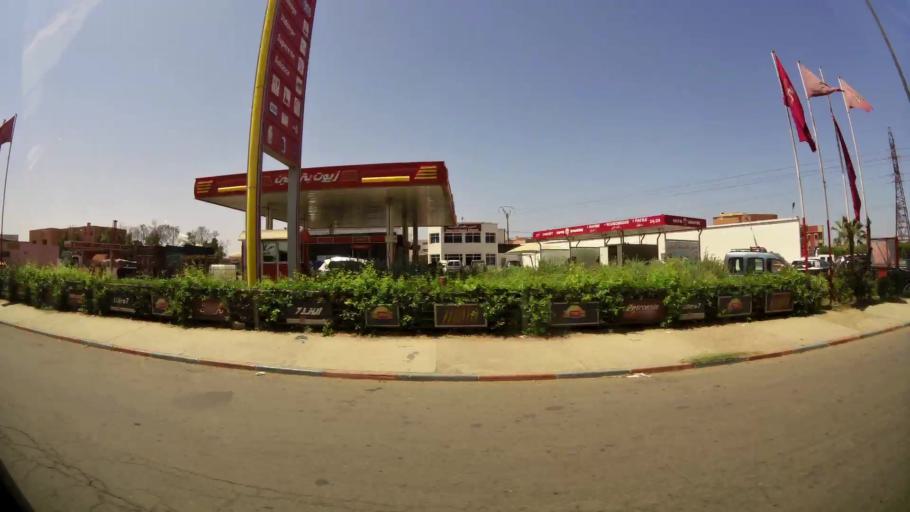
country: MA
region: Souss-Massa-Draa
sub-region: Inezgane-Ait Mellou
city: Inezgane
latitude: 30.3369
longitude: -9.4936
